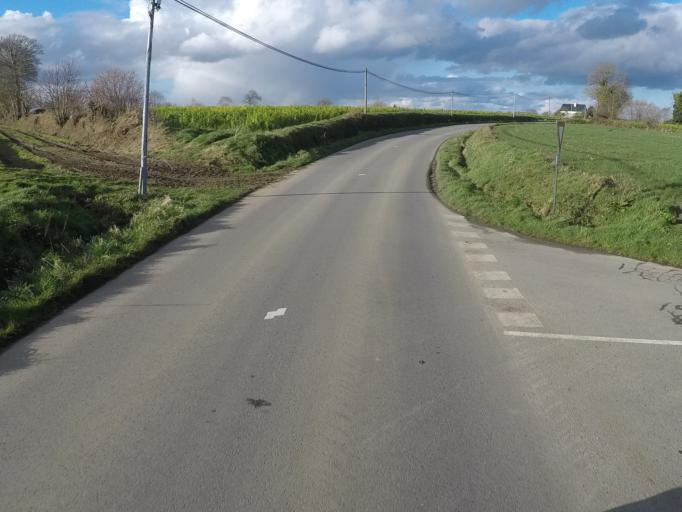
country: FR
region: Brittany
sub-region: Departement des Cotes-d'Armor
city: Plouagat
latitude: 48.5576
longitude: -2.9806
